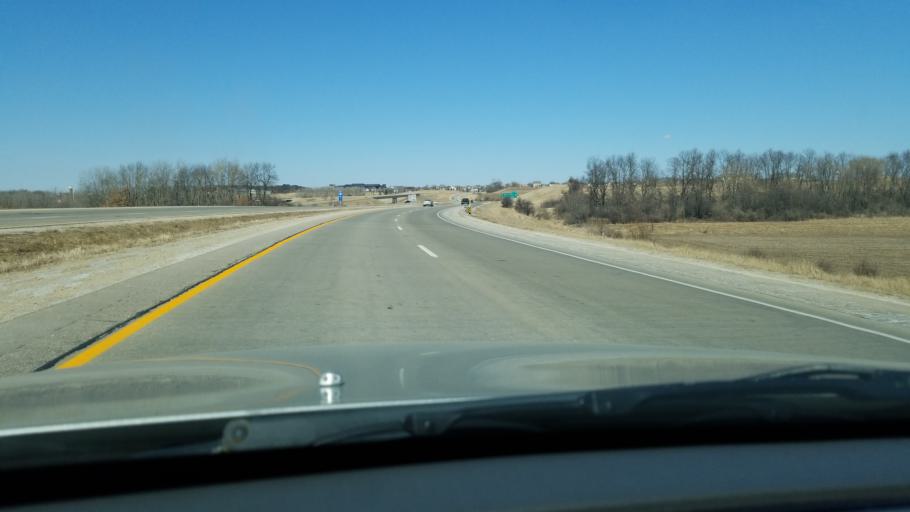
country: US
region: Wisconsin
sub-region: Dane County
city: Verona
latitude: 42.9786
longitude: -89.5563
